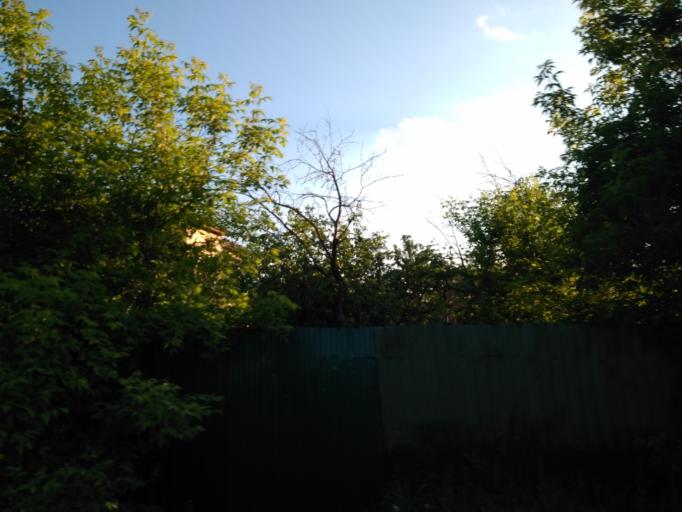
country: RU
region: Moskovskaya
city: Zhukovskiy
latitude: 55.5772
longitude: 38.1111
